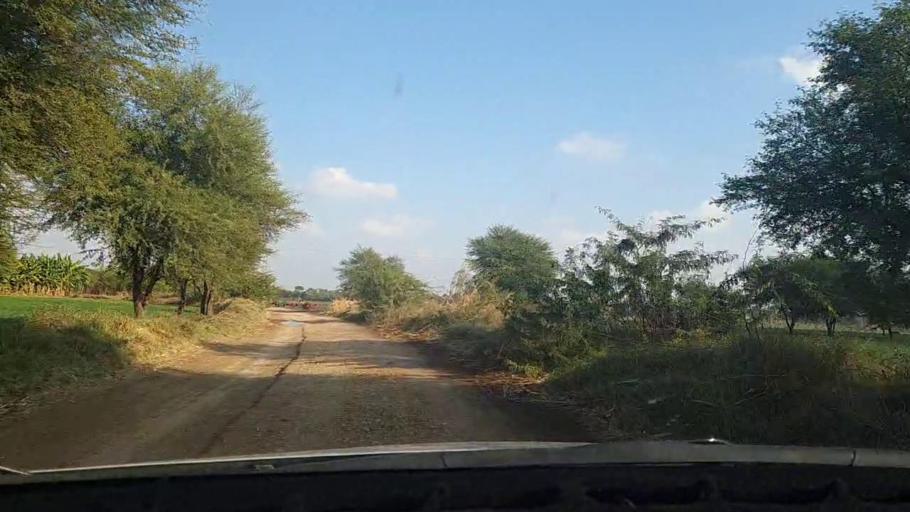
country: PK
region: Sindh
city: Tando Mittha Khan
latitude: 25.8836
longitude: 69.2892
